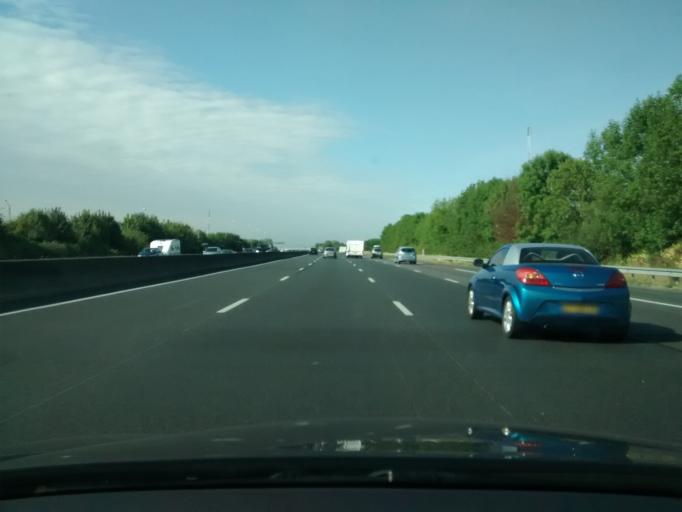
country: FR
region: Ile-de-France
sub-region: Departement de l'Essonne
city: Fontenay-les-Briis
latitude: 48.6357
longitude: 2.1477
